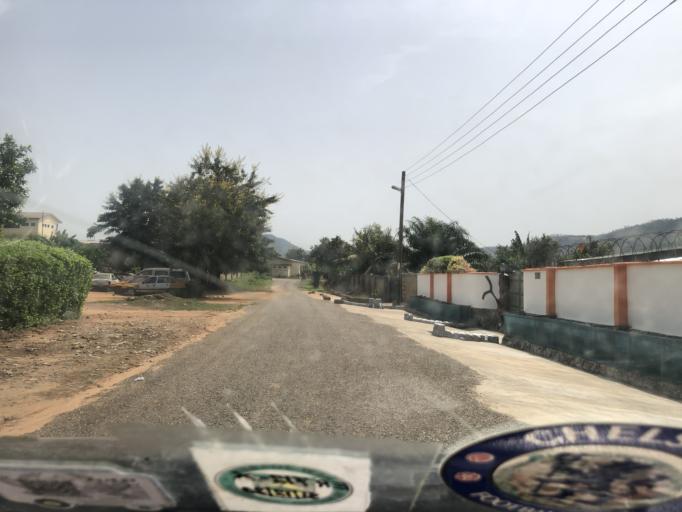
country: GH
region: Eastern
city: Koforidua
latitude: 6.0947
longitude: -0.2712
